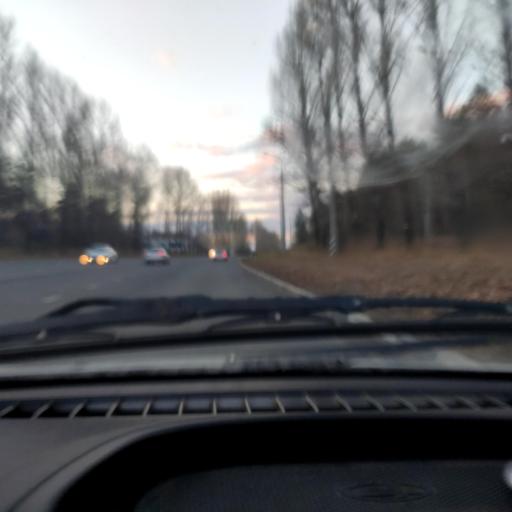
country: RU
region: Samara
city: Zhigulevsk
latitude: 53.5058
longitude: 49.4664
